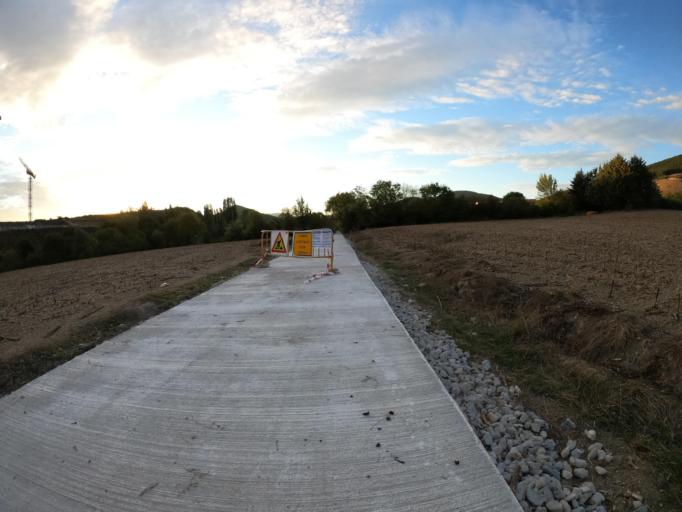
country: ES
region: Navarre
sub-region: Provincia de Navarra
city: Egues-Uharte
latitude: 42.8329
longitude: -1.5756
